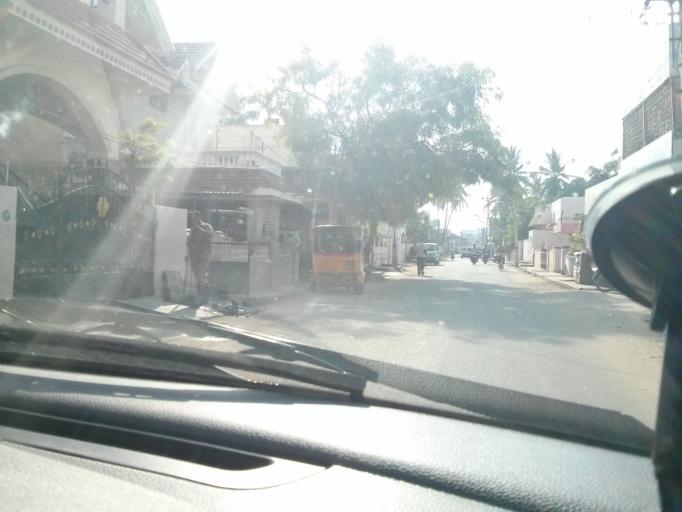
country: IN
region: Tamil Nadu
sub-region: Coimbatore
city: Coimbatore
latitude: 11.0335
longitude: 76.9468
